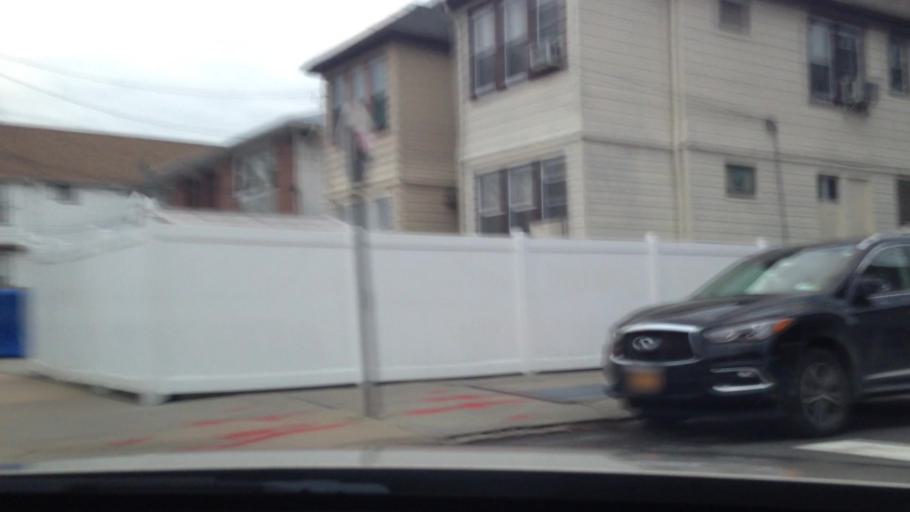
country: US
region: New York
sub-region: Queens County
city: Jamaica
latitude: 40.7589
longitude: -73.8071
